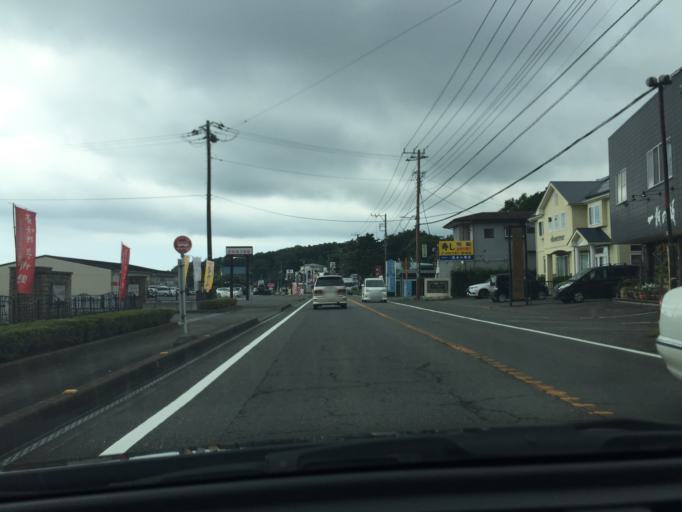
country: JP
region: Shizuoka
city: Ito
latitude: 34.9144
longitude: 139.1202
